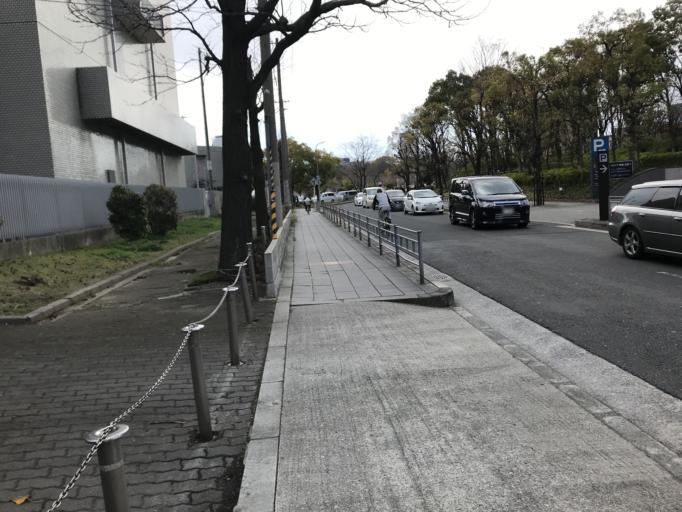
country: JP
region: Osaka
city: Osaka-shi
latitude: 34.6919
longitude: 135.5292
